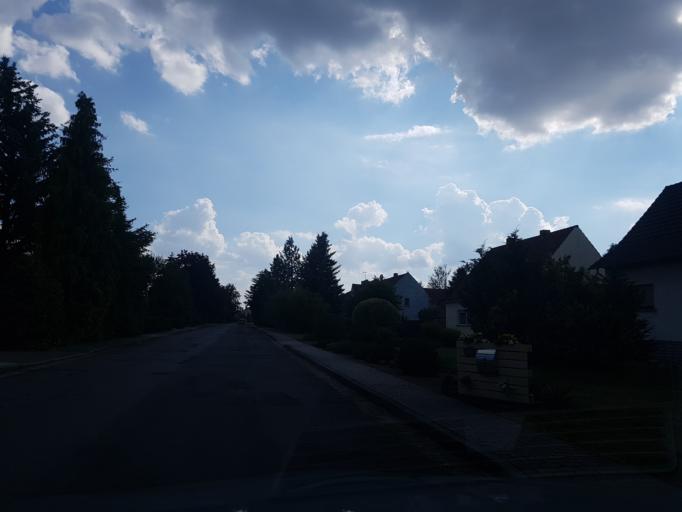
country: DE
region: Brandenburg
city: Schlieben
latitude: 51.6877
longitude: 13.3541
